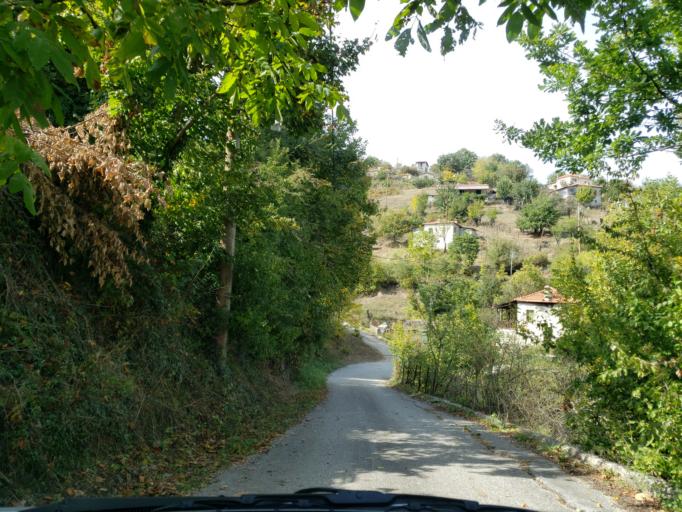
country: GR
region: Thessaly
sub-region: Trikala
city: Kastraki
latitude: 39.7764
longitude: 21.6605
